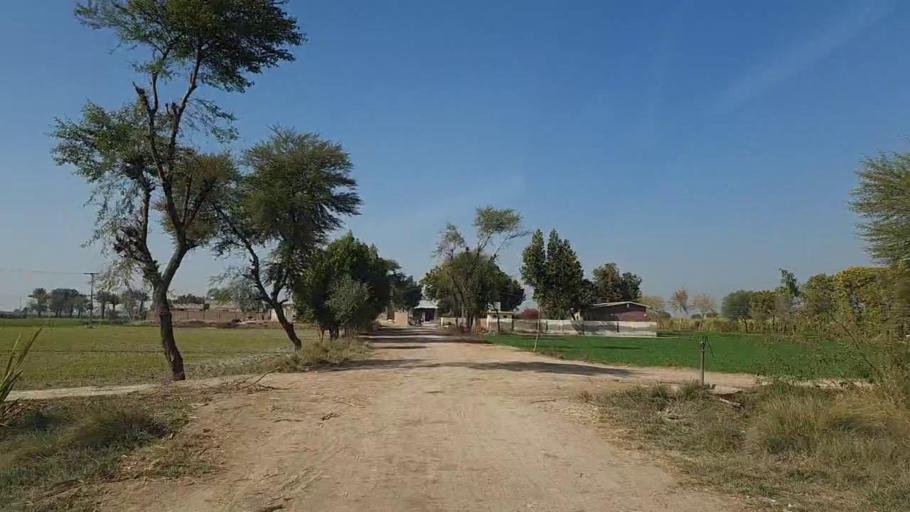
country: PK
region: Sindh
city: Nawabshah
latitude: 26.2824
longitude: 68.3726
